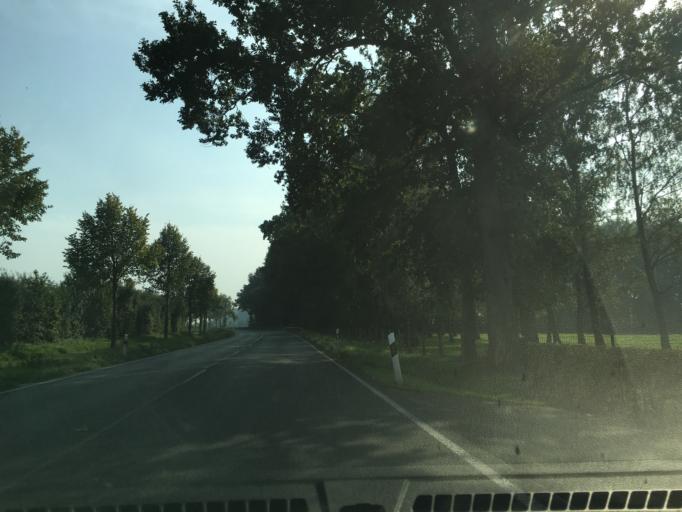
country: DE
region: North Rhine-Westphalia
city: Olfen
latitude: 51.7775
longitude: 7.3697
